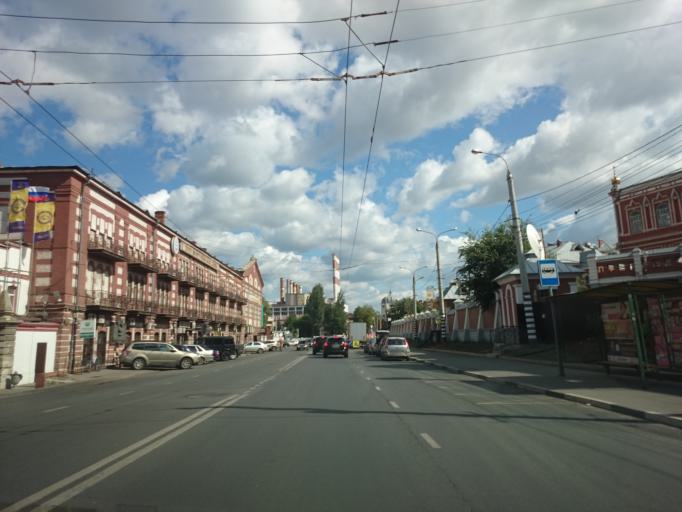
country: RU
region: Samara
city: Samara
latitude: 53.2000
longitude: 50.0980
